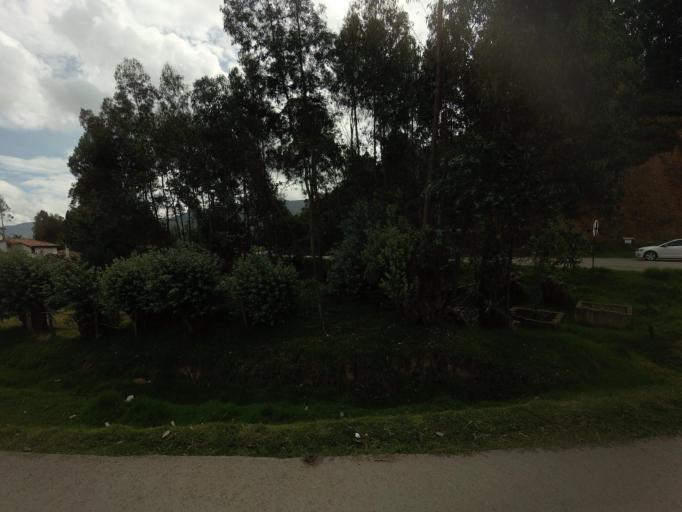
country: CO
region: Boyaca
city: Tibasosa
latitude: 5.7787
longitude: -72.9799
